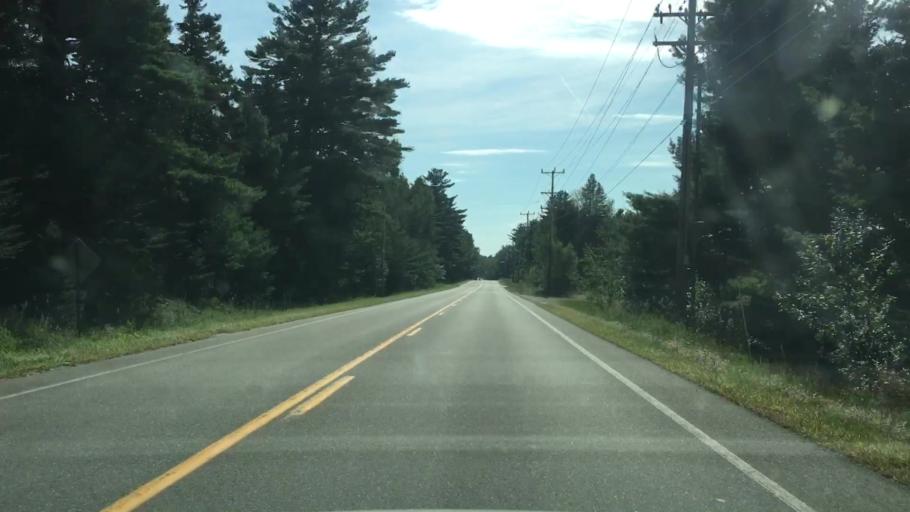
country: US
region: Maine
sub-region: Penobscot County
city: Lincoln
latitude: 45.3920
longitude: -68.5306
